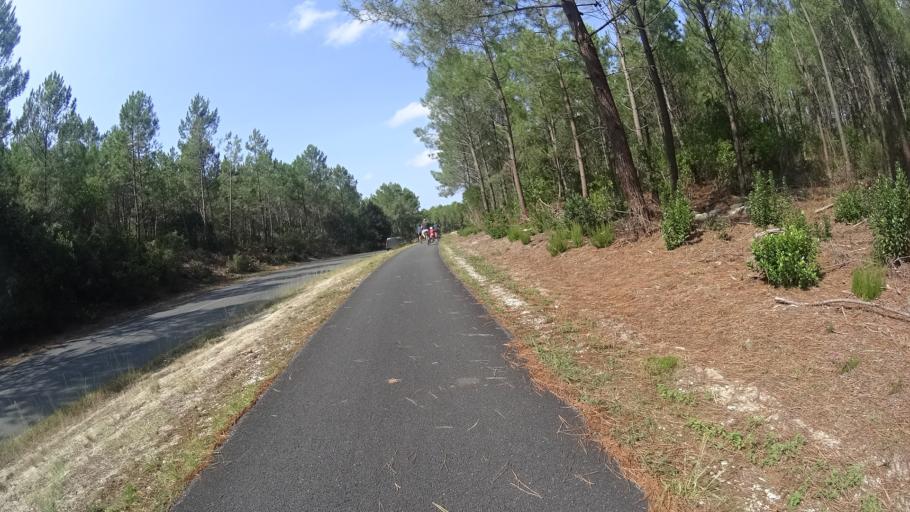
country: FR
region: Aquitaine
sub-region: Departement de la Gironde
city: Lacanau
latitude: 44.9831
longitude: -1.1434
